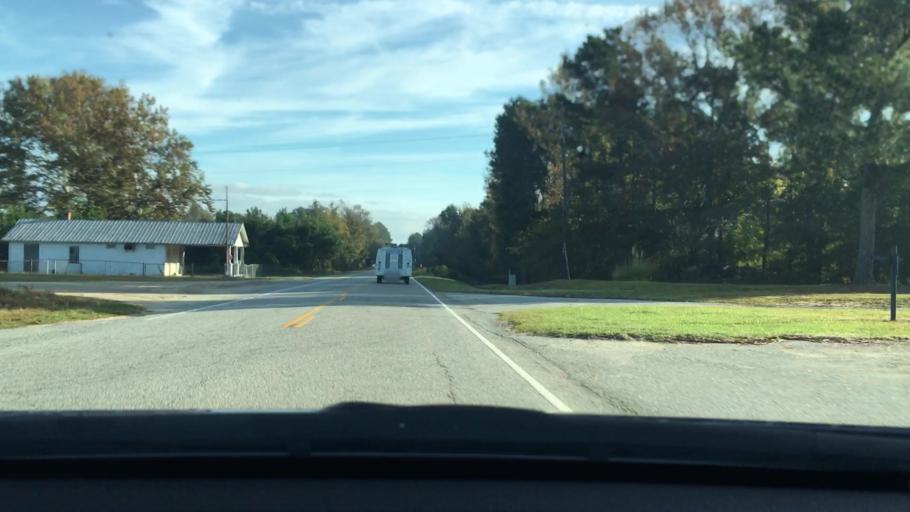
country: US
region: South Carolina
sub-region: Lee County
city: Bishopville
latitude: 34.0744
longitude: -80.2061
